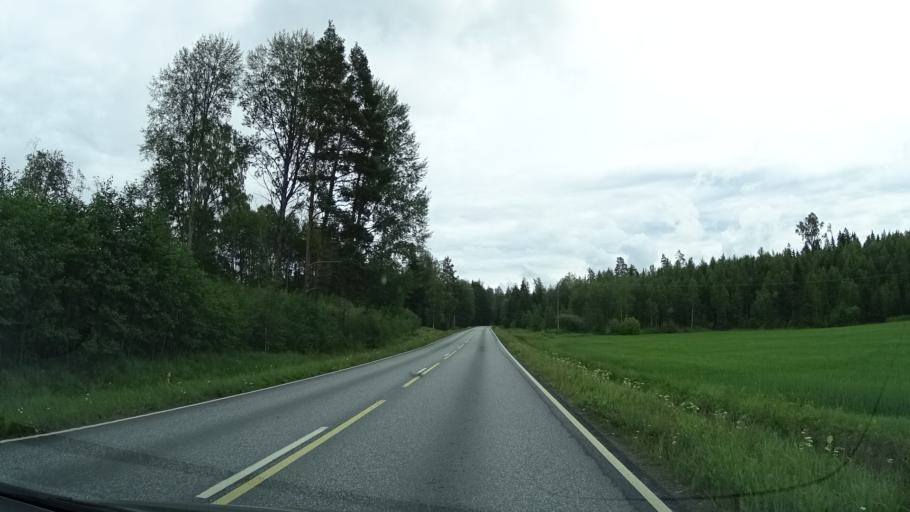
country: FI
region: Pirkanmaa
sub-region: Etelae-Pirkanmaa
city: Urjala
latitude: 61.0914
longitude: 23.3887
